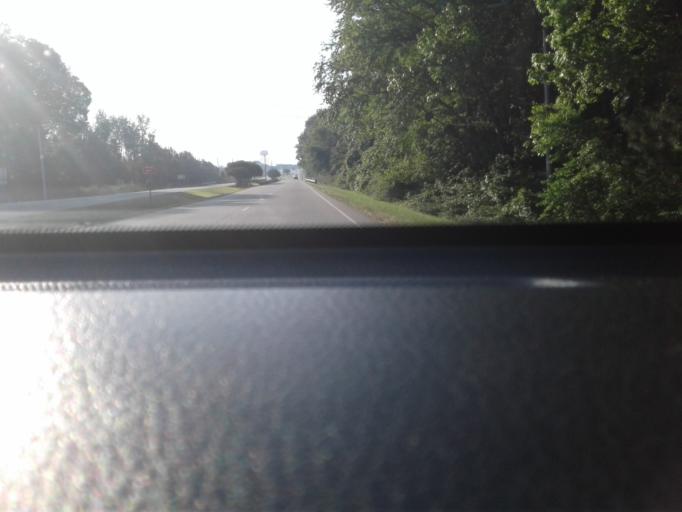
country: US
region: North Carolina
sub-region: Harnett County
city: Erwin
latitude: 35.3230
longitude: -78.6440
